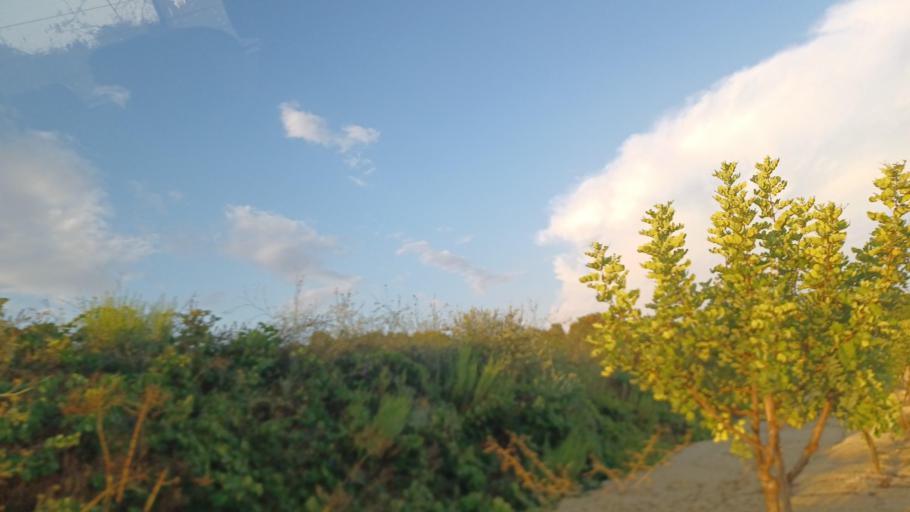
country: CY
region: Pafos
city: Tala
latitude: 34.8994
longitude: 32.4991
